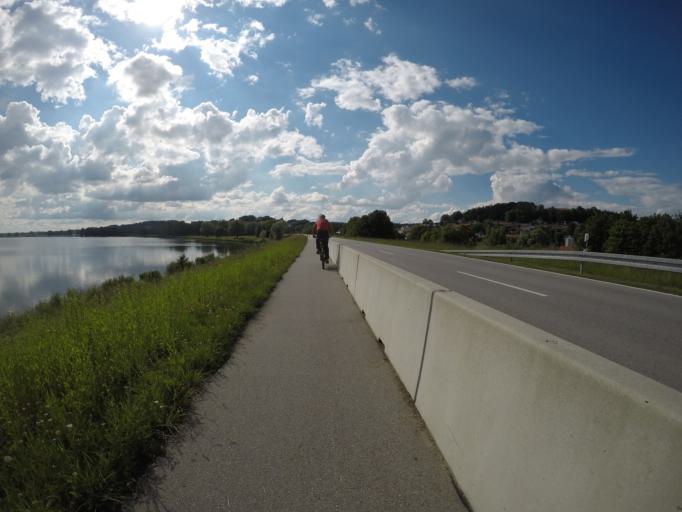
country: DE
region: Bavaria
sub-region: Lower Bavaria
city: Marklkofen
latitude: 48.5703
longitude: 12.5892
